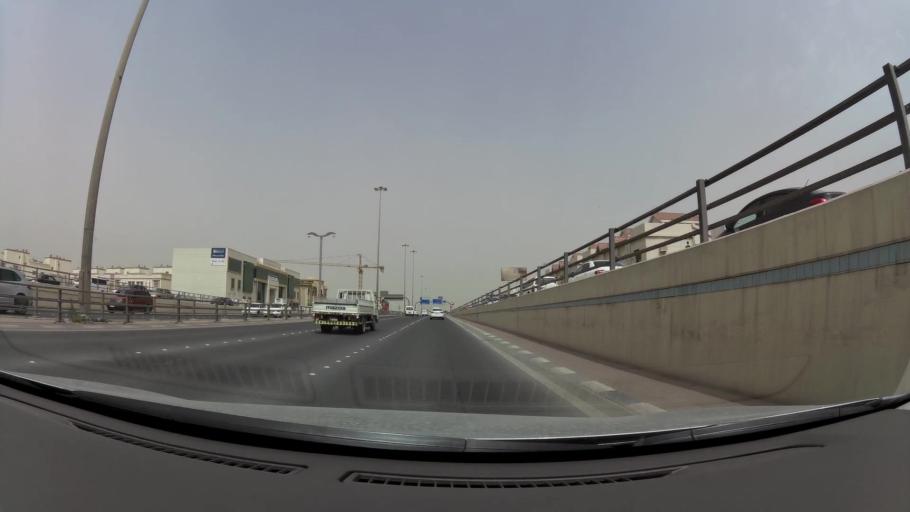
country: QA
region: Baladiyat ad Dawhah
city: Doha
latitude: 25.2671
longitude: 51.4951
